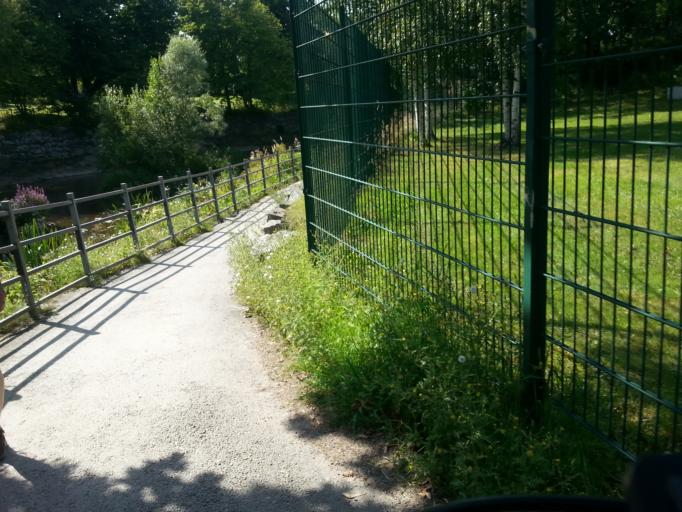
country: FI
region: Uusimaa
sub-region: Helsinki
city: Helsinki
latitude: 60.2170
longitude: 24.9831
